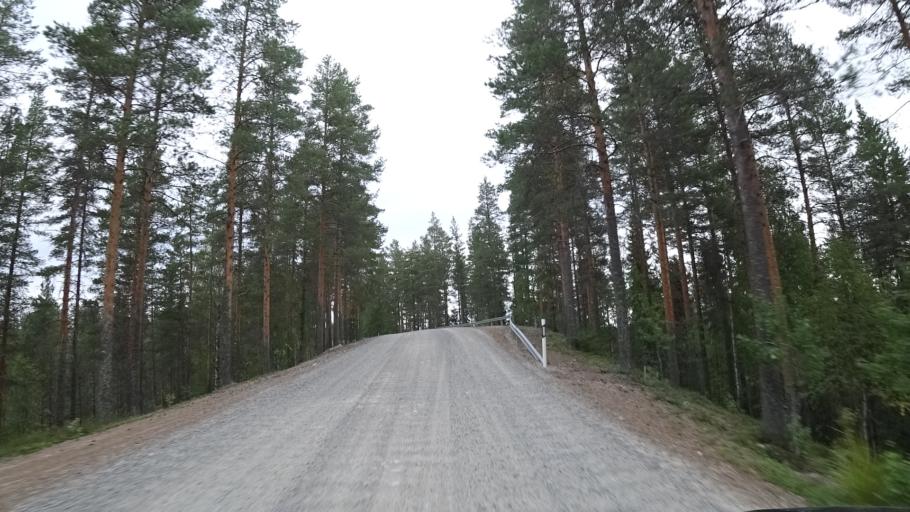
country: FI
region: North Karelia
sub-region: Pielisen Karjala
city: Lieksa
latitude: 63.2612
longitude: 30.3215
